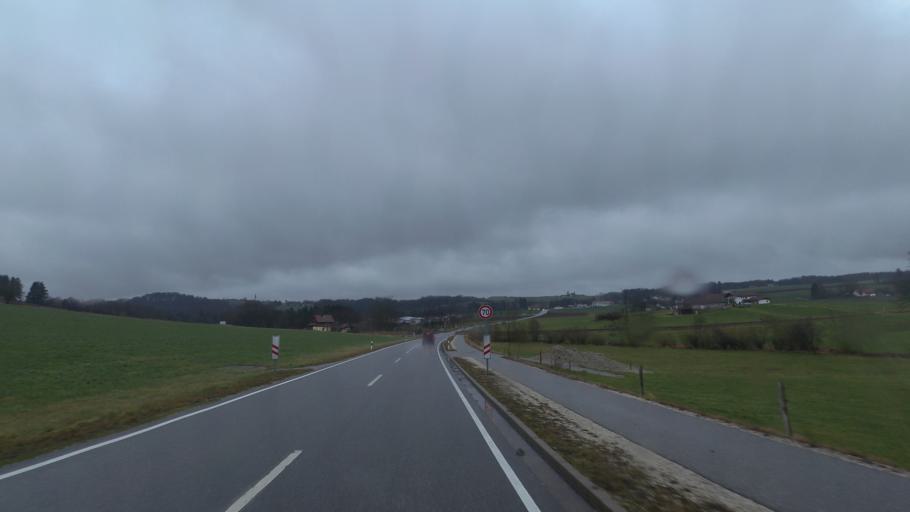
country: DE
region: Bavaria
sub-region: Upper Bavaria
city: Sankt Leonhard am Wonneberg
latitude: 47.9308
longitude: 12.7019
